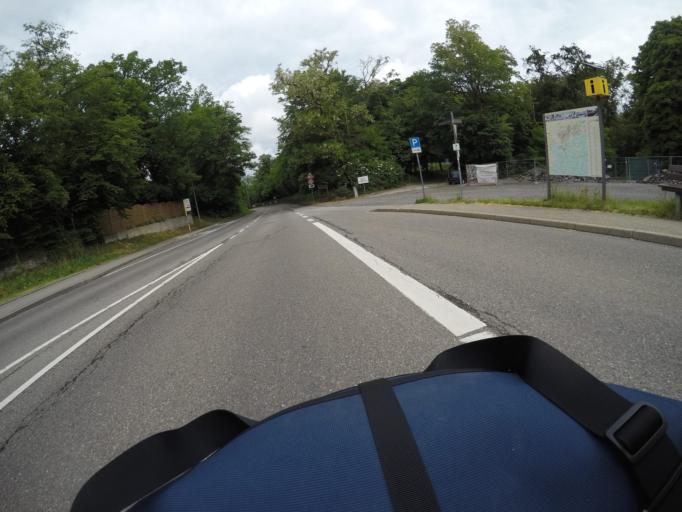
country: DE
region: Baden-Wuerttemberg
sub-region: Regierungsbezirk Stuttgart
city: Gerlingen
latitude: 48.7891
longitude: 9.0660
